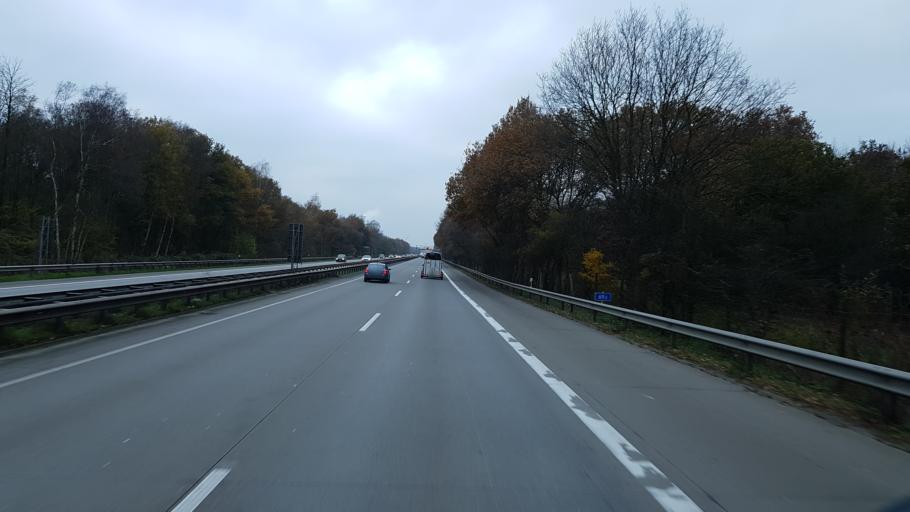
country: DE
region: Bremen
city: Bremen
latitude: 53.1156
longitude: 8.8471
